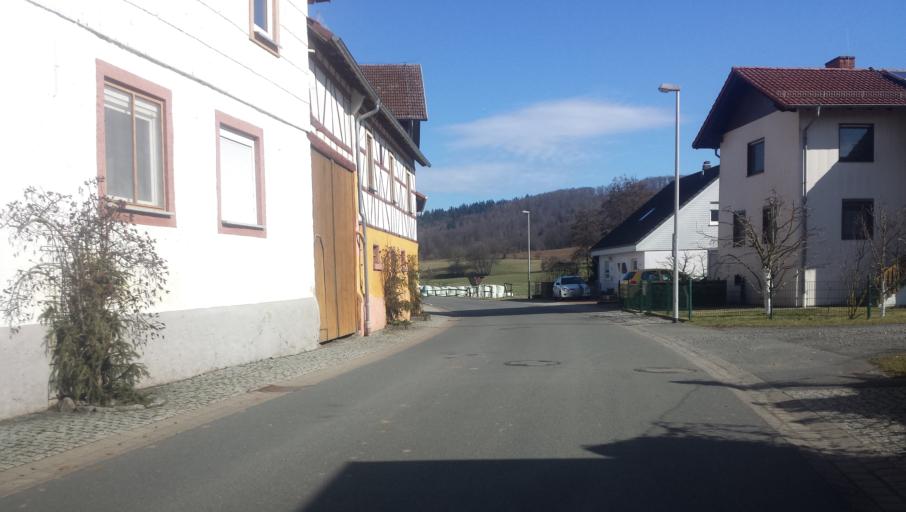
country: DE
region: Hesse
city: Lutzelbach
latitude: 49.7601
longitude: 8.7678
